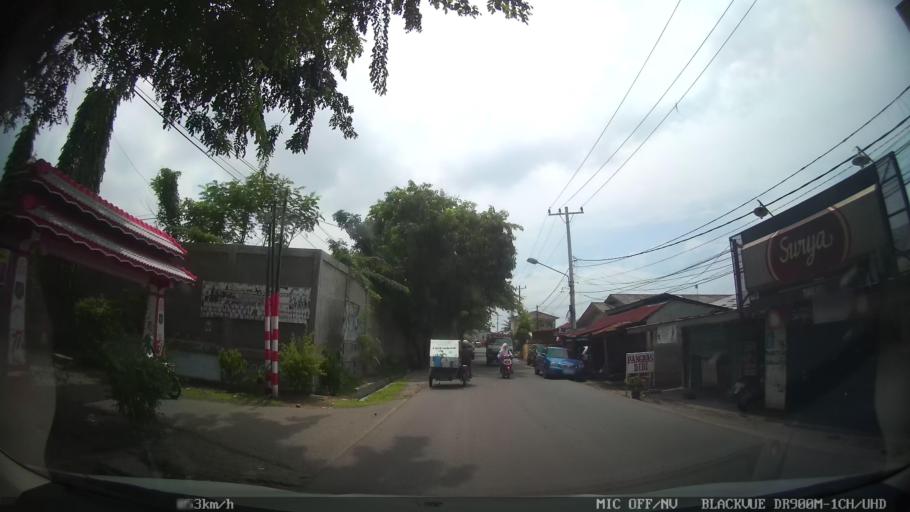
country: ID
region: North Sumatra
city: Medan
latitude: 3.6430
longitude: 98.6693
